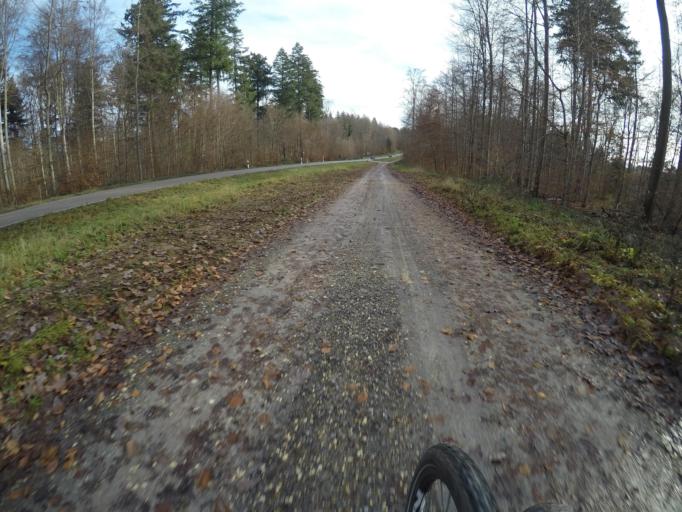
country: DE
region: Baden-Wuerttemberg
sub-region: Regierungsbezirk Stuttgart
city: Winterbach
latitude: 48.7660
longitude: 9.4824
